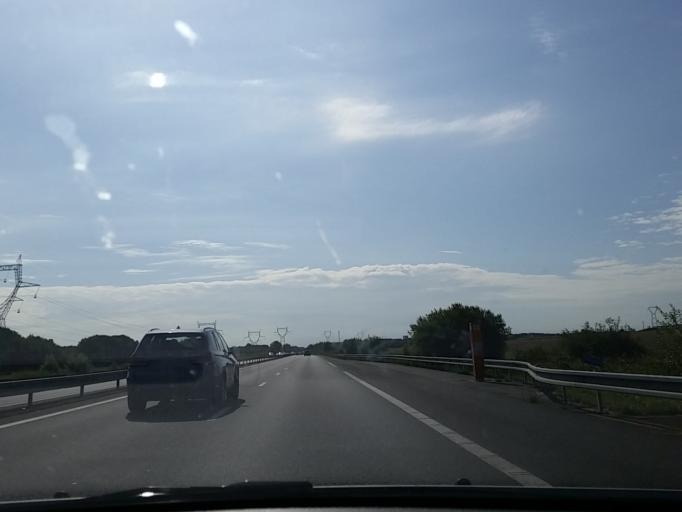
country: FR
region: Centre
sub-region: Departement du Cher
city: La Chapelle-Saint-Ursin
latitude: 47.0663
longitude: 2.2905
